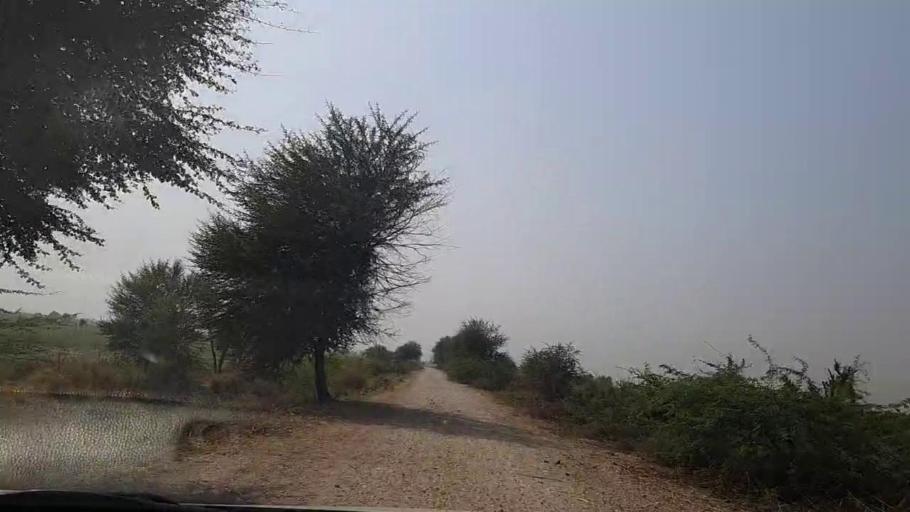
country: PK
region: Sindh
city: Pithoro
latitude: 25.5911
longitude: 69.2361
